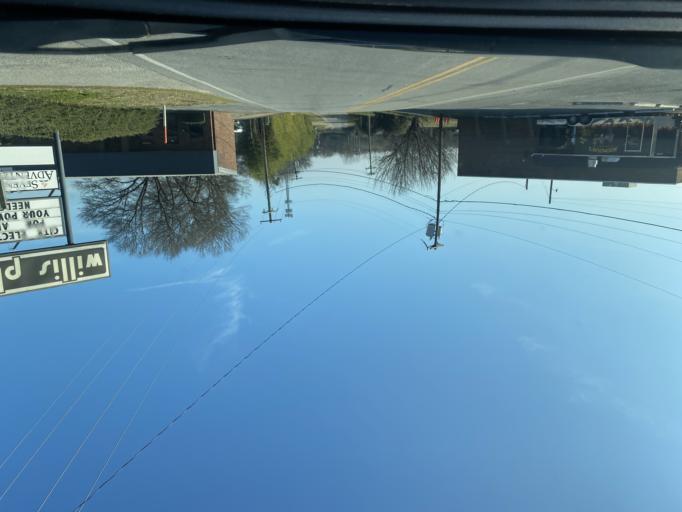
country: US
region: South Carolina
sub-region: Cherokee County
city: Gaffney
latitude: 35.0658
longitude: -81.6620
